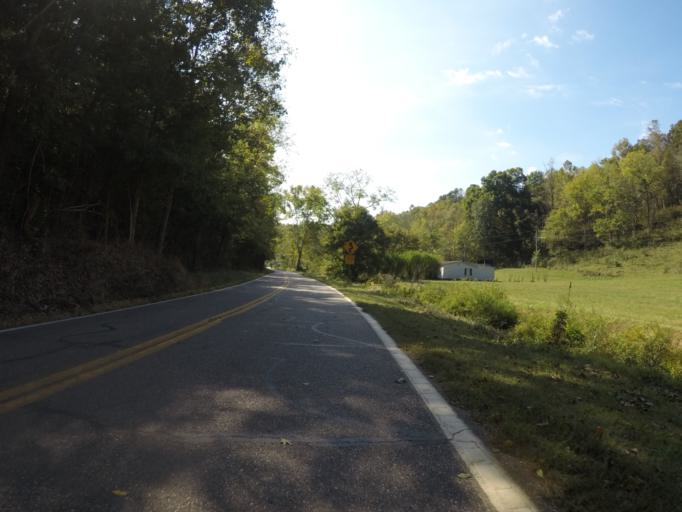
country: US
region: West Virginia
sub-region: Cabell County
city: Lesage
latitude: 38.6390
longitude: -82.4325
